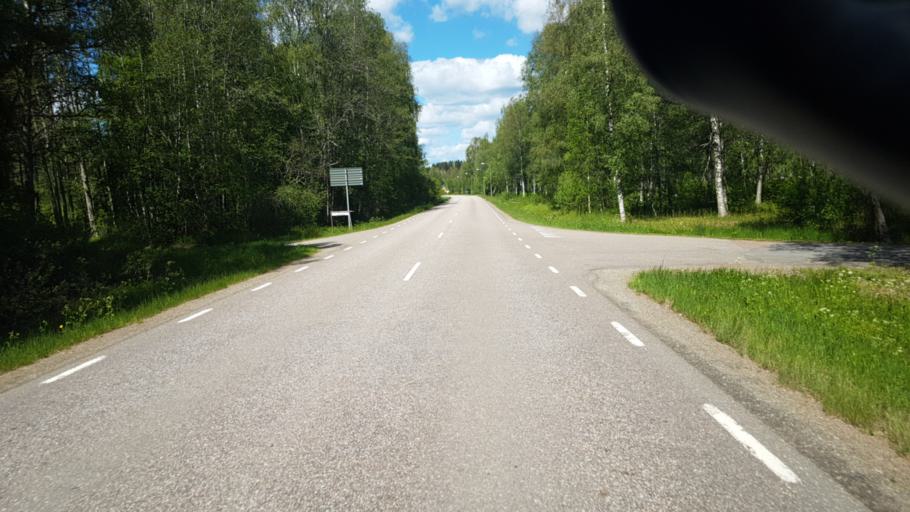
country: SE
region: Vaermland
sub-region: Arvika Kommun
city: Arvika
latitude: 59.6578
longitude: 12.8874
